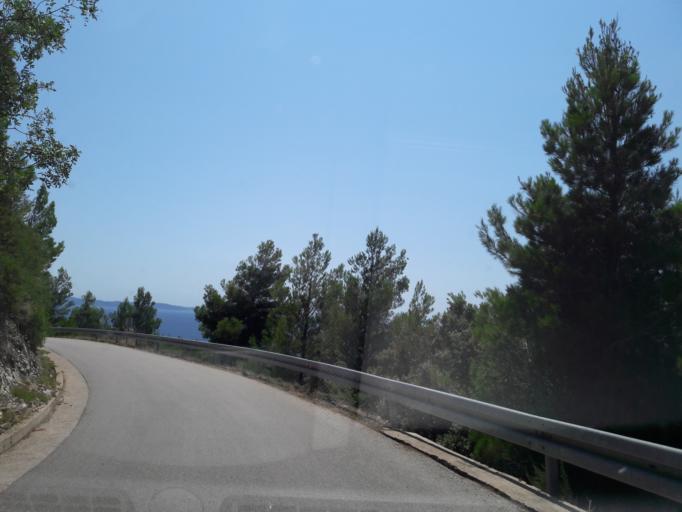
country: HR
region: Dubrovacko-Neretvanska
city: Blato
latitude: 42.9094
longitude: 17.4217
